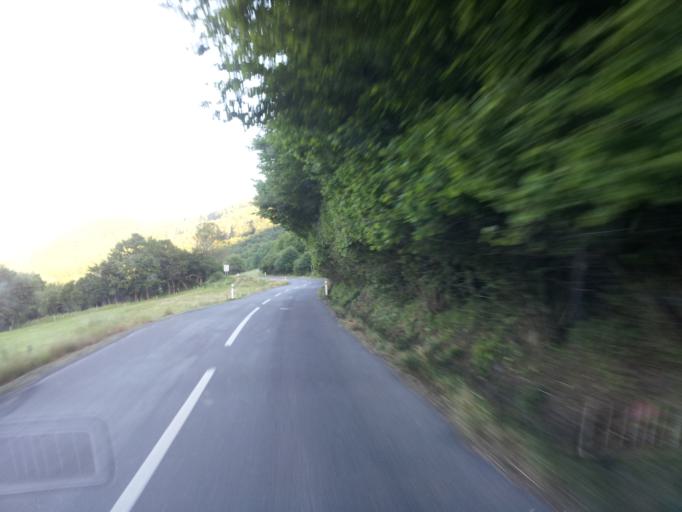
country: SK
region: Banskobystricky
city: Svaety Anton
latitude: 48.3374
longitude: 18.9516
